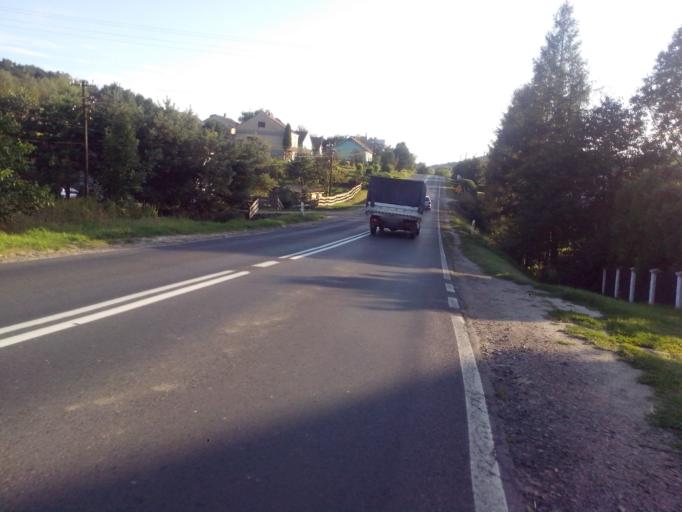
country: PL
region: Subcarpathian Voivodeship
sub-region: Powiat strzyzowski
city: Strzyzow
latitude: 49.8922
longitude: 21.8287
